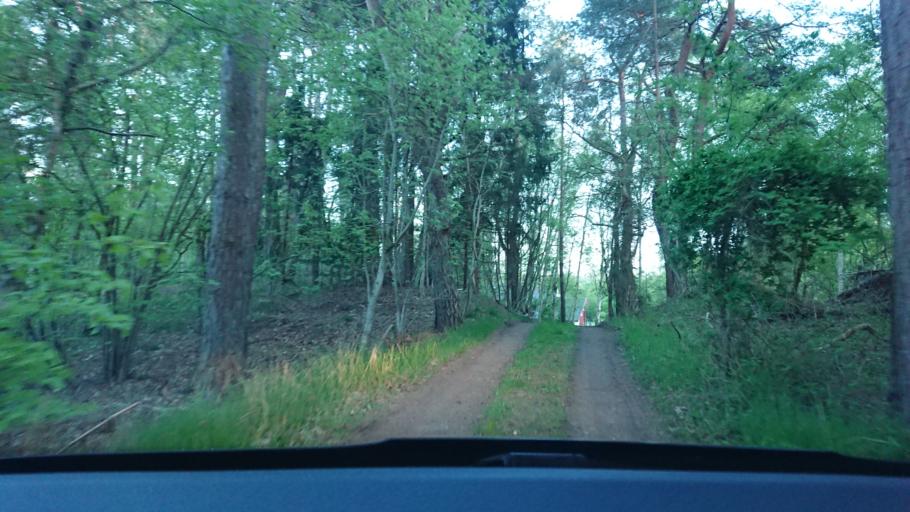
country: DK
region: Zealand
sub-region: Odsherred Kommune
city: Nykobing Sjaelland
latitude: 55.9403
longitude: 11.6973
